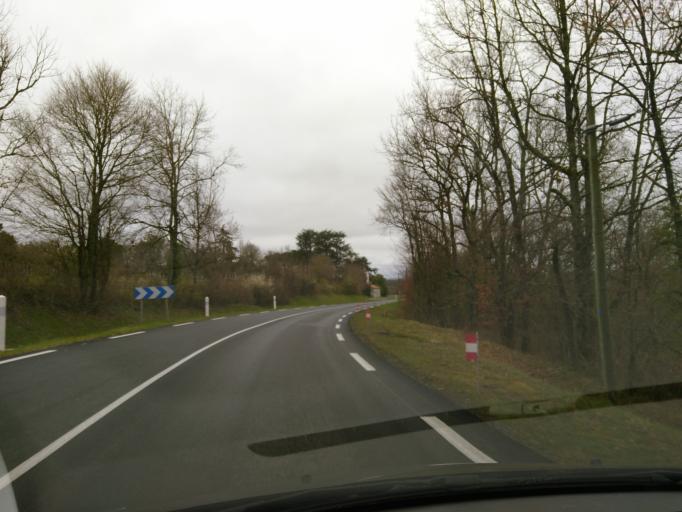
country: FR
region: Aquitaine
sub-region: Departement de la Dordogne
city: Monbazillac
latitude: 44.7392
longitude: 0.5413
